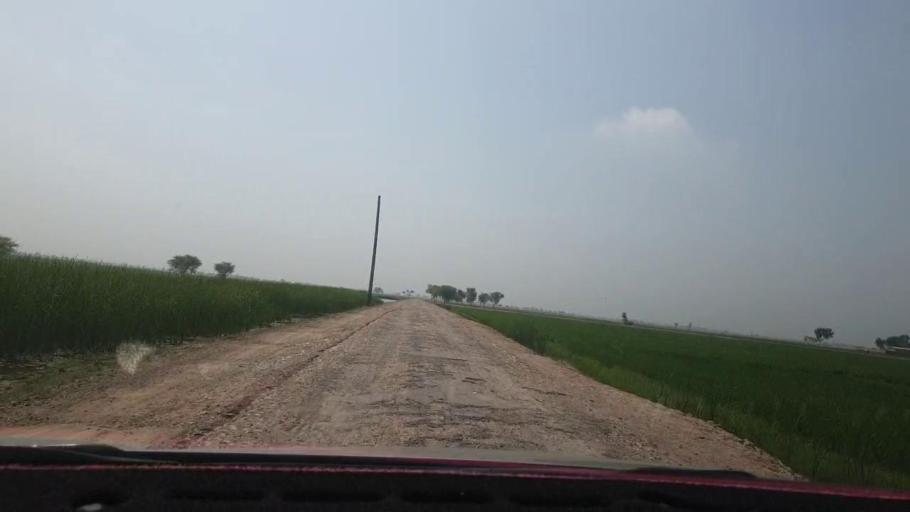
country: PK
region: Sindh
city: Warah
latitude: 27.4005
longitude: 67.8489
